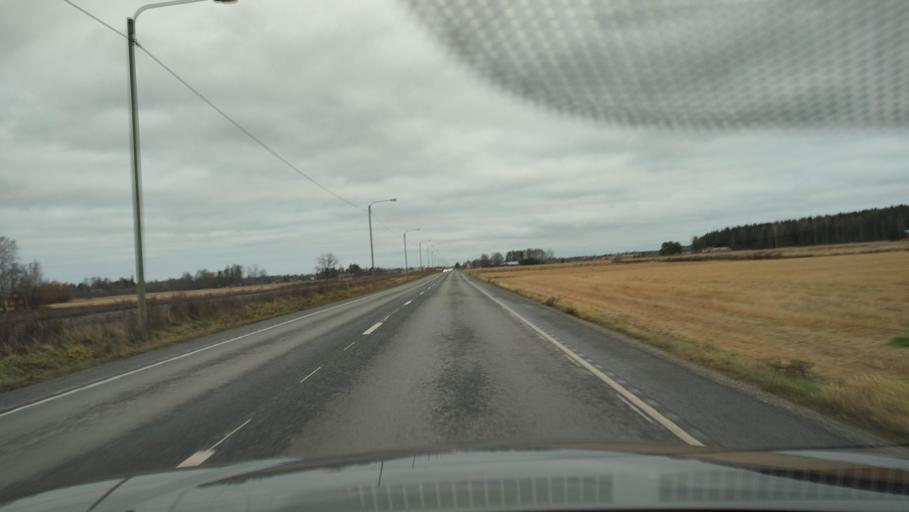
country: FI
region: Southern Ostrobothnia
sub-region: Seinaejoki
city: Ilmajoki
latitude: 62.7091
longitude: 22.5345
